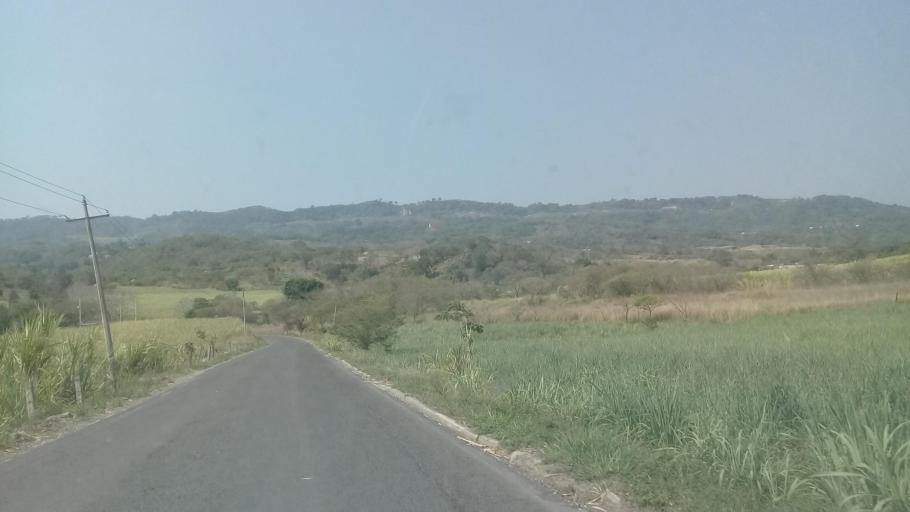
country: MX
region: Veracruz
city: El Castillo
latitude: 19.5823
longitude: -96.8285
